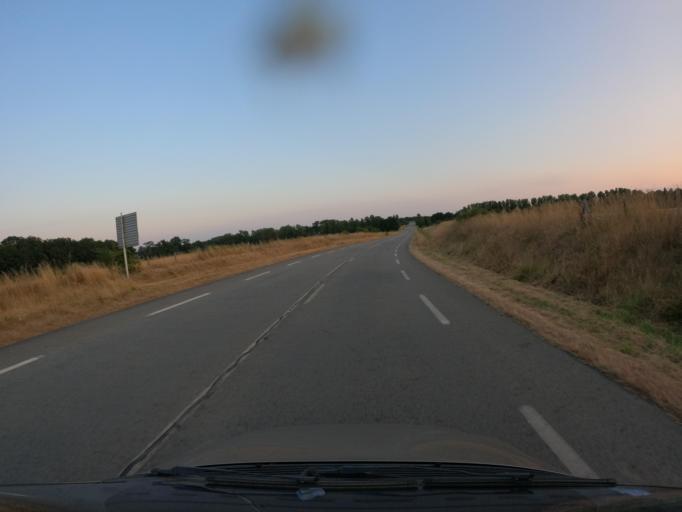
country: FR
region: Pays de la Loire
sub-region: Departement de la Mayenne
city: Chemaze
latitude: 47.7927
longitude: -0.7613
